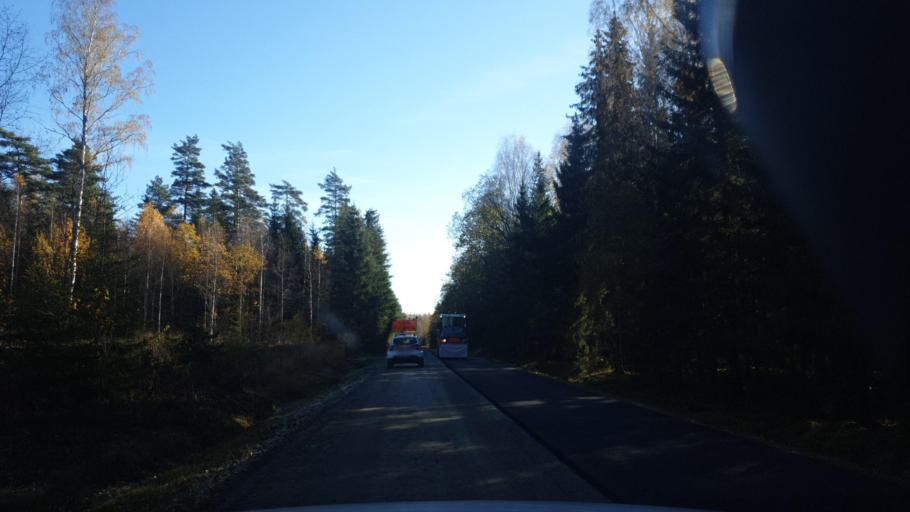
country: SE
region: Vaermland
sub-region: Karlstads Kommun
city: Valberg
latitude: 59.4127
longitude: 13.1692
